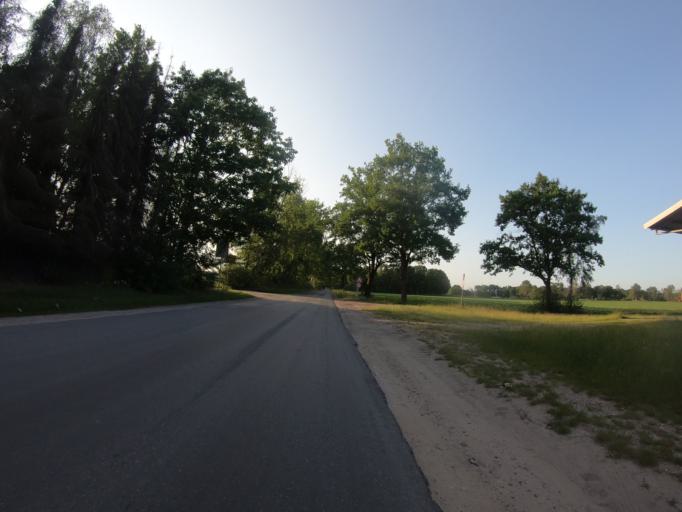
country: DE
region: Lower Saxony
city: Wagenhoff
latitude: 52.5146
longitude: 10.4807
